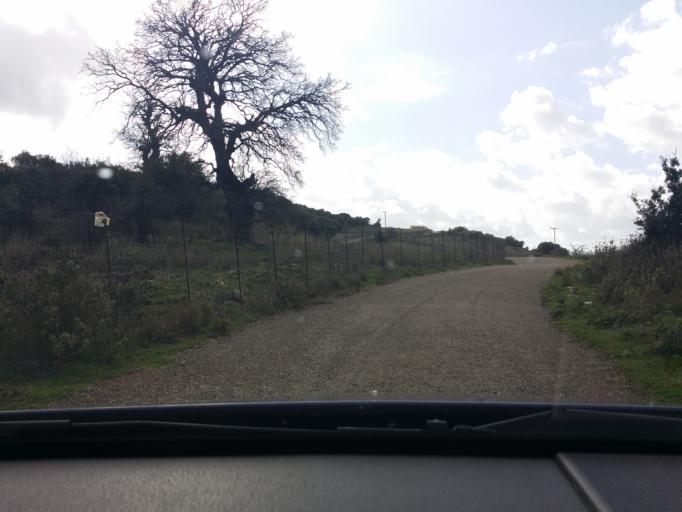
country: GR
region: West Greece
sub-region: Nomos Aitolias kai Akarnanias
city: Fitiai
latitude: 38.6692
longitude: 21.1907
